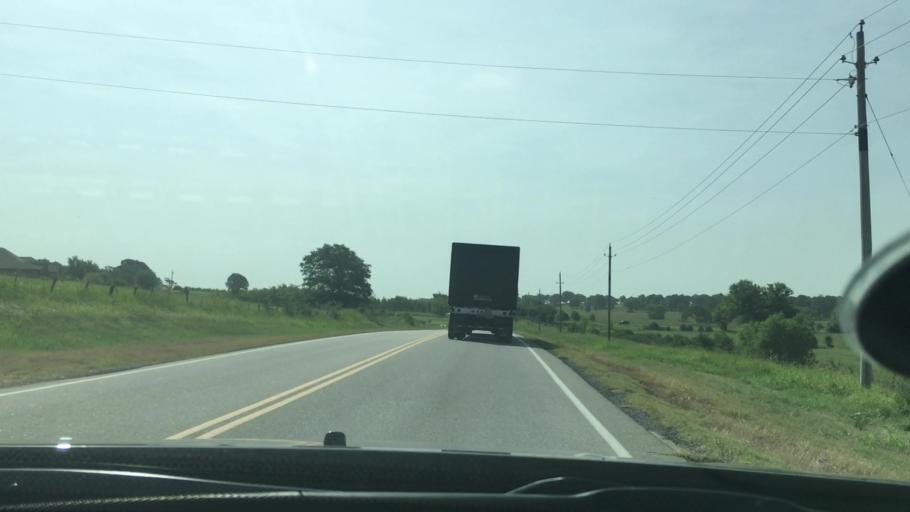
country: US
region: Oklahoma
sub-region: Atoka County
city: Atoka
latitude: 34.4013
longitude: -96.1742
